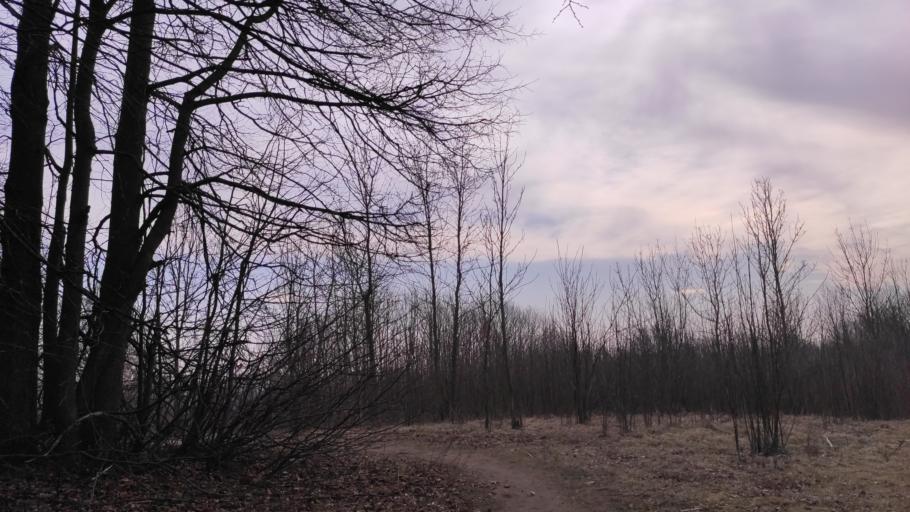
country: BY
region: Minsk
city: Novoye Medvezhino
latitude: 53.8878
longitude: 27.4687
